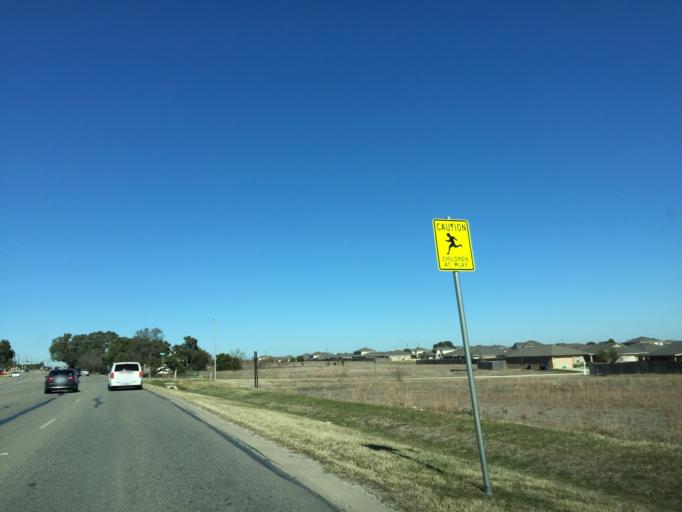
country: US
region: Texas
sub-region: Williamson County
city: Leander
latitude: 30.5650
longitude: -97.8647
